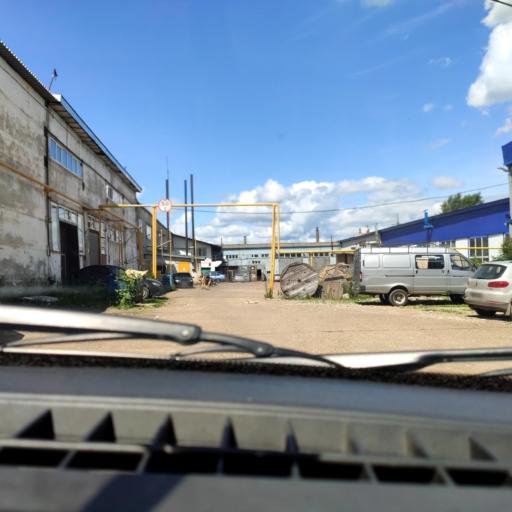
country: RU
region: Bashkortostan
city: Ufa
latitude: 54.8382
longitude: 56.1140
